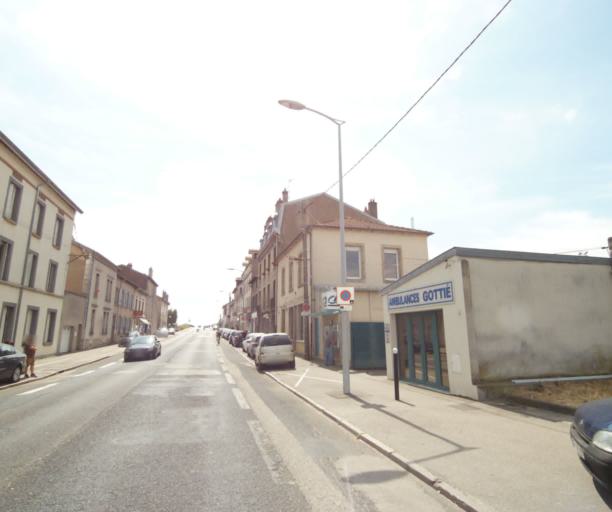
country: FR
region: Lorraine
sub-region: Departement de Meurthe-et-Moselle
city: Luneville
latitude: 48.5894
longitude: 6.5060
